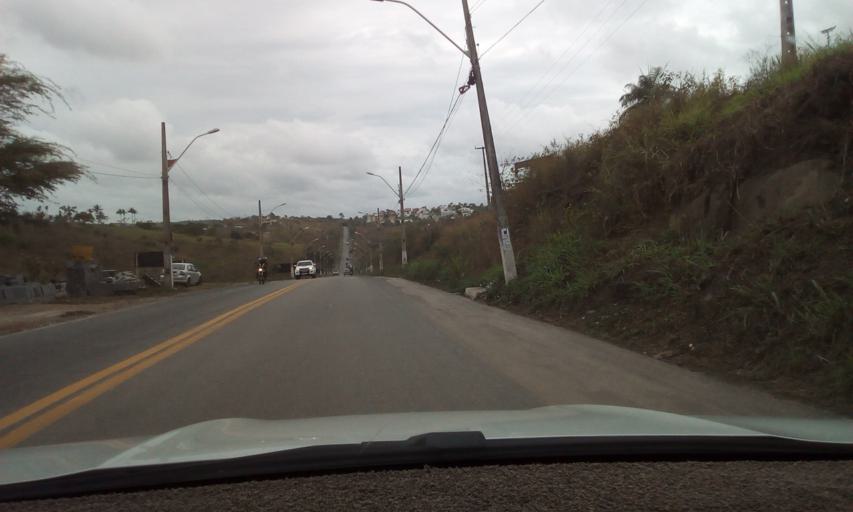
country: BR
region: Paraiba
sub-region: Campina Grande
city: Campina Grande
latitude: -7.1976
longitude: -35.8776
